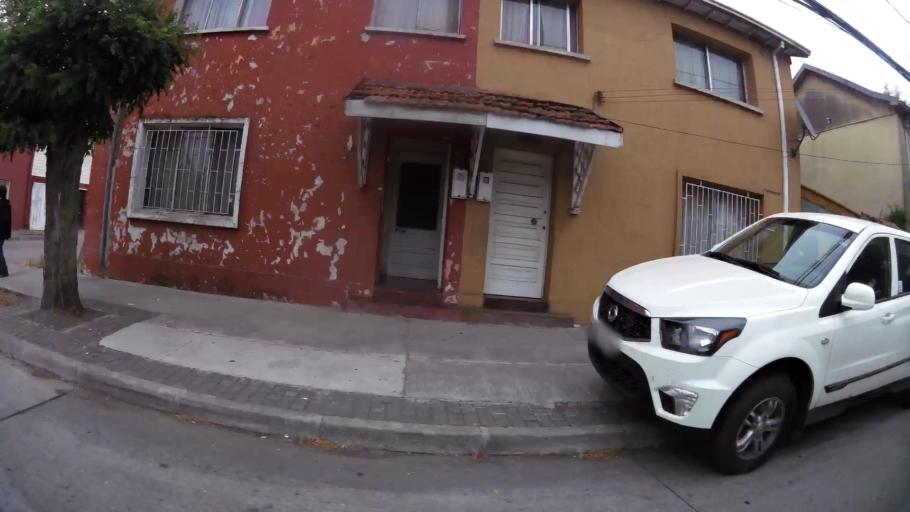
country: CL
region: Biobio
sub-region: Provincia de Concepcion
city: Concepcion
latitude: -36.8121
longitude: -73.0326
